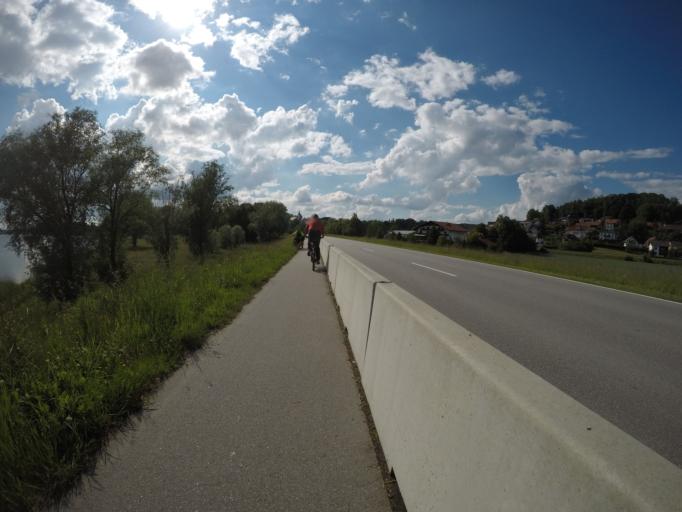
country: DE
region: Bavaria
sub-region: Lower Bavaria
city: Marklkofen
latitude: 48.5711
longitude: 12.5867
